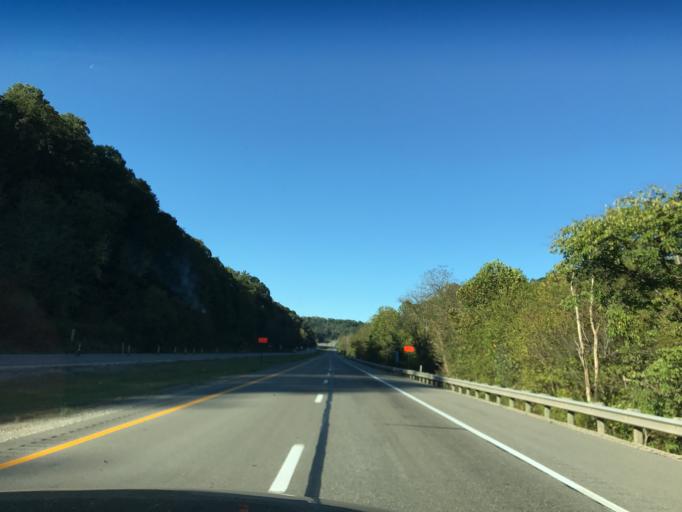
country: US
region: Ohio
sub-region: Washington County
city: Reno
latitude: 39.2470
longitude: -81.3862
